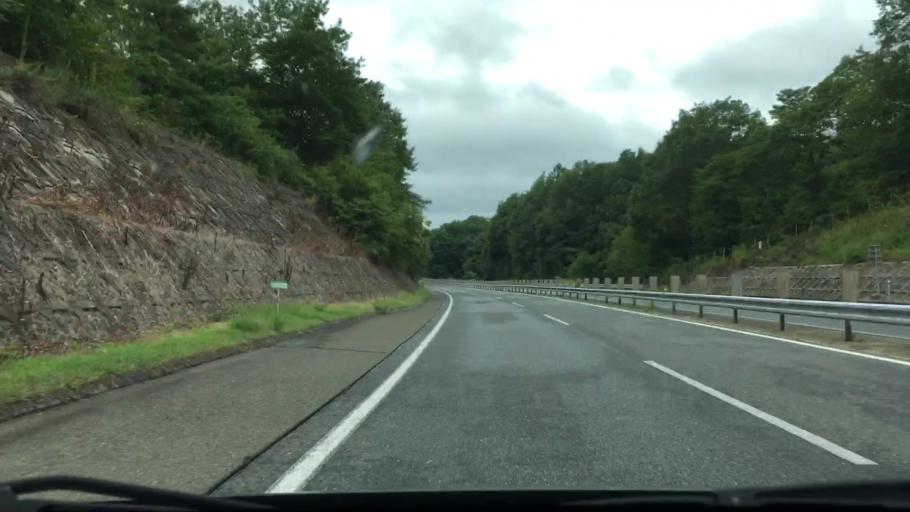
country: JP
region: Hiroshima
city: Shobara
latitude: 34.8412
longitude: 133.0407
